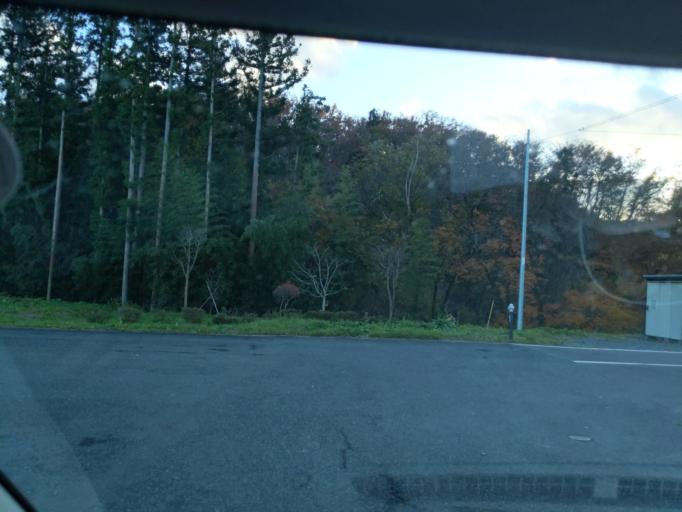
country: JP
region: Iwate
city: Mizusawa
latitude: 39.0433
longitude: 141.0478
